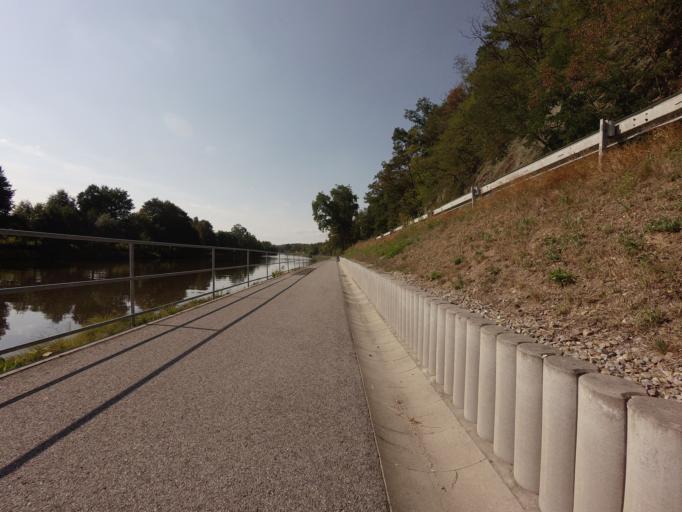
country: CZ
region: Jihocesky
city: Tyn nad Vltavou
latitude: 49.2120
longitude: 14.4411
